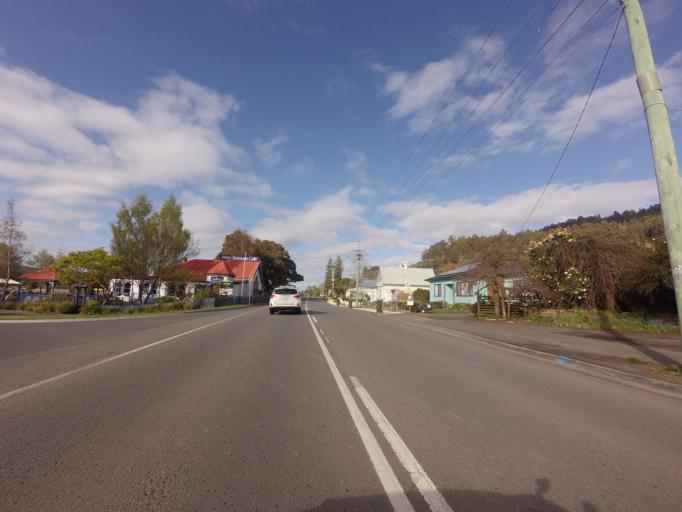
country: AU
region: Tasmania
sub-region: Huon Valley
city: Franklin
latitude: -43.0929
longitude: 147.0085
